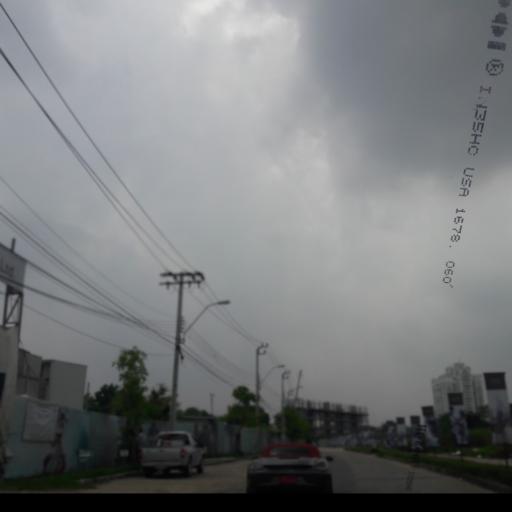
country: TH
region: Bangkok
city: Suan Luang
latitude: 13.7307
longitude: 100.6220
